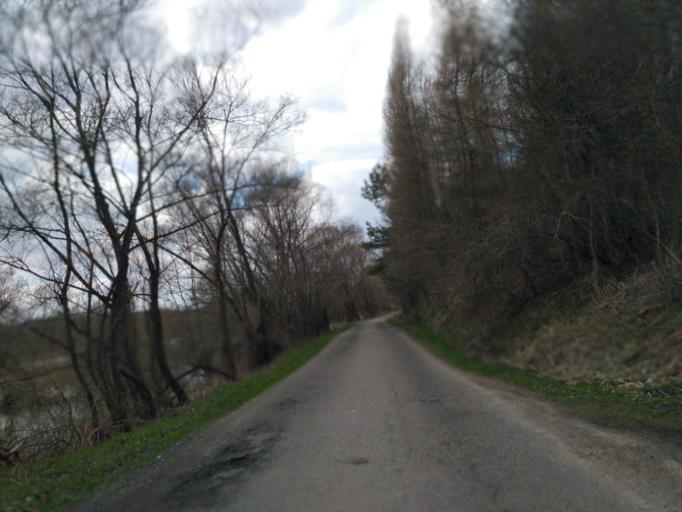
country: PL
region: Subcarpathian Voivodeship
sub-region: Powiat sanocki
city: Tyrawa Woloska
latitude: 49.6617
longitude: 22.2978
